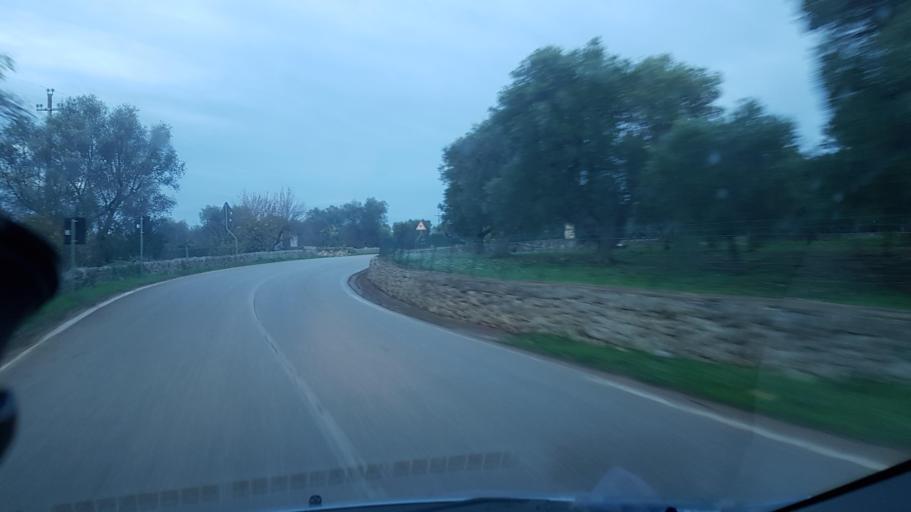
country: IT
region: Apulia
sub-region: Provincia di Brindisi
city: Ceglie Messapica
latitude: 40.6446
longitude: 17.5513
